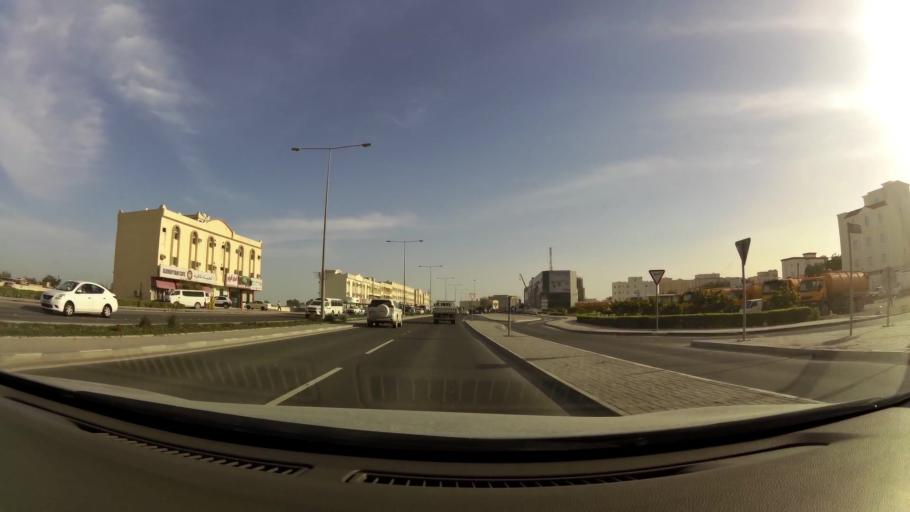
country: QA
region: Al Wakrah
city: Al Wakrah
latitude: 25.1656
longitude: 51.6077
